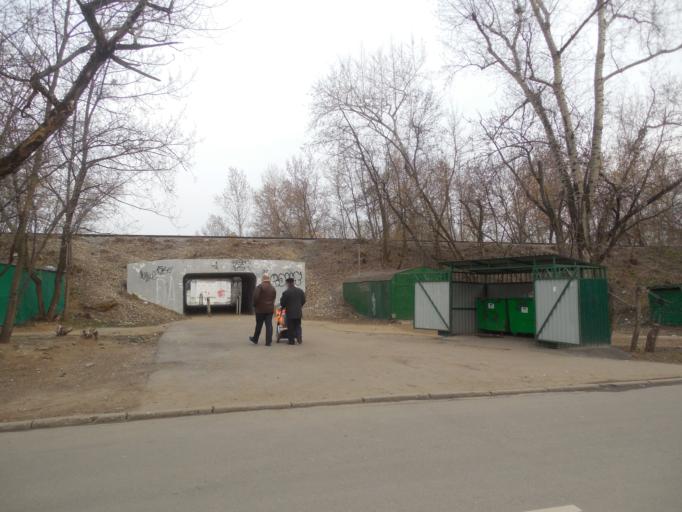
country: RU
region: Moscow
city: Ryazanskiy
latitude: 55.7301
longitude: 37.7589
